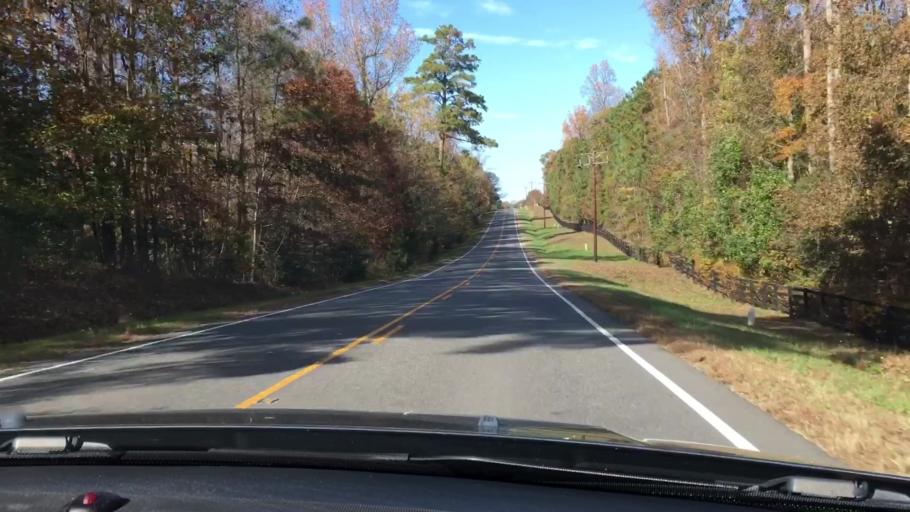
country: US
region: Virginia
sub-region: King and Queen County
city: King and Queen Court House
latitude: 37.6005
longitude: -76.9068
